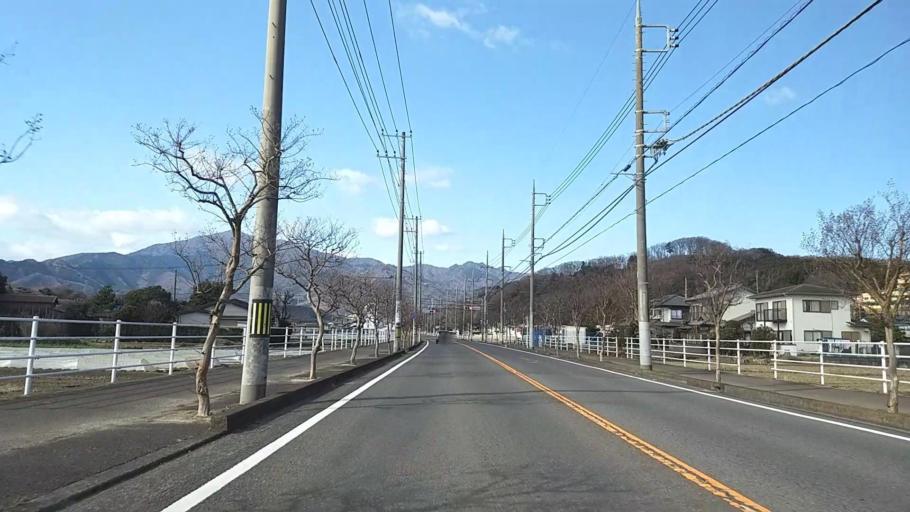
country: JP
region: Kanagawa
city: Atsugi
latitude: 35.4325
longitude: 139.3253
